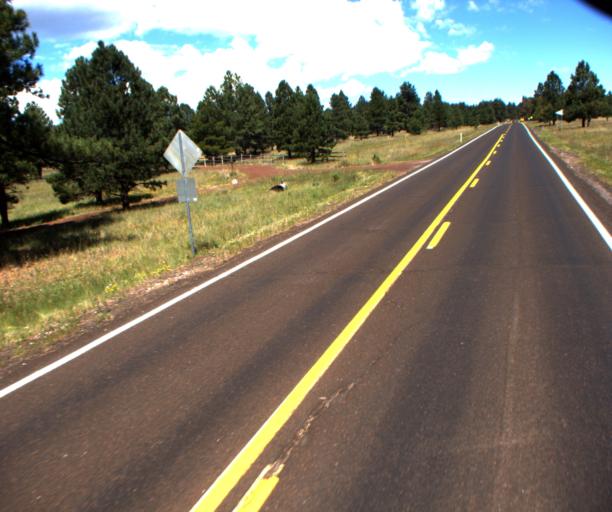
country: US
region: Arizona
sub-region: Apache County
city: Eagar
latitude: 34.0654
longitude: -109.4641
